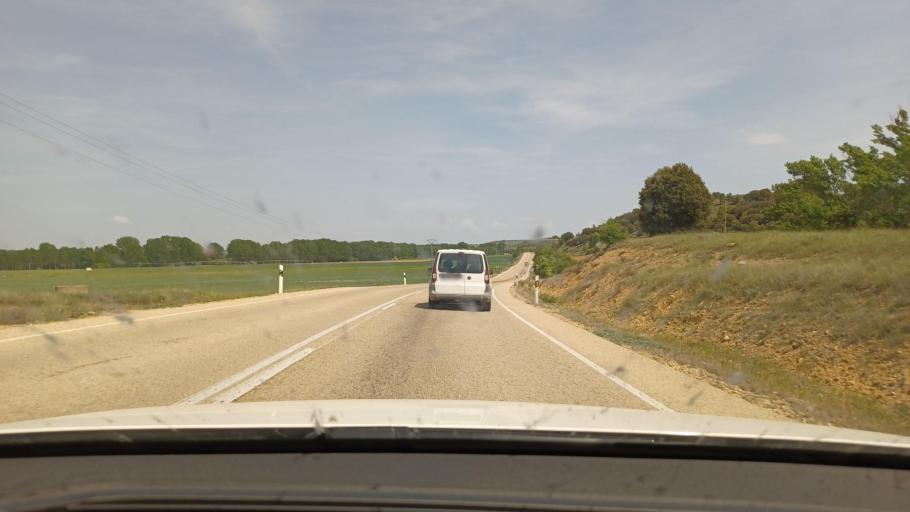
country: ES
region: Castille and Leon
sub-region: Provincia de Soria
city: Barca
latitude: 41.4731
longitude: -2.5978
